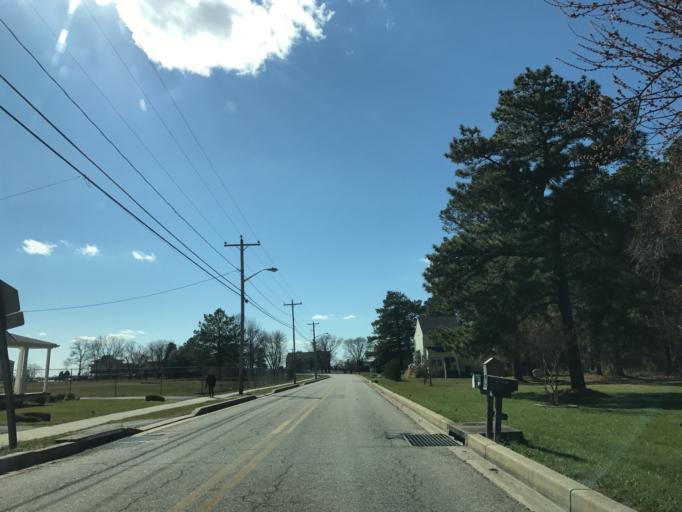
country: US
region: Maryland
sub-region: Kent County
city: Rock Hall
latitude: 39.1356
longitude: -76.2387
